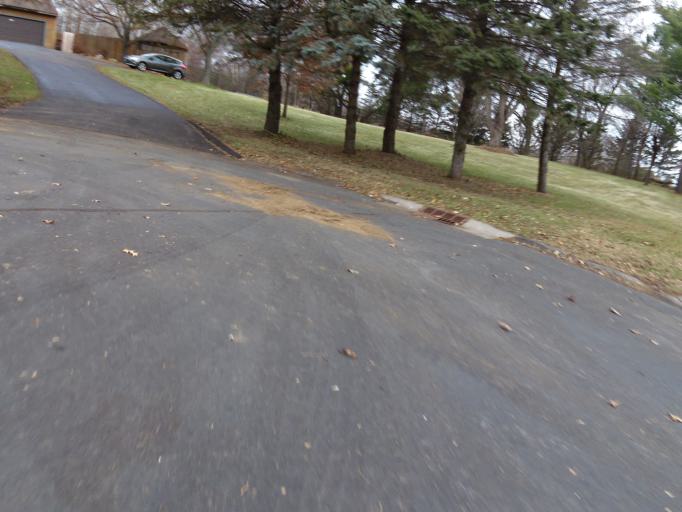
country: US
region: Minnesota
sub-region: Washington County
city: Lake Elmo
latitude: 44.9848
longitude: -92.8687
